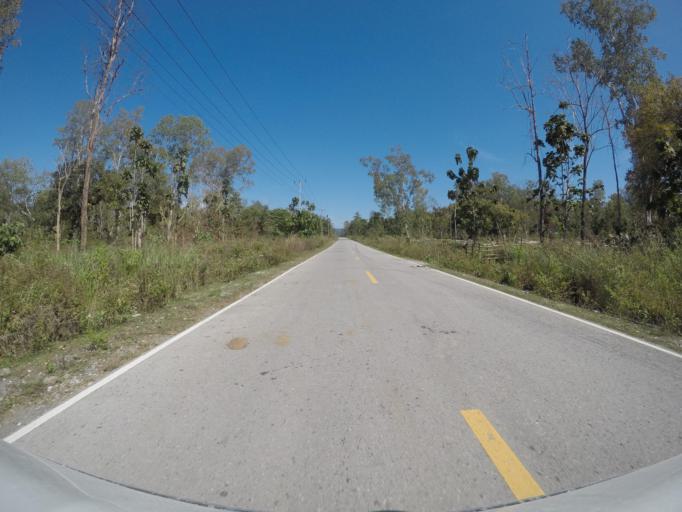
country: TL
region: Viqueque
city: Viqueque
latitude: -8.9717
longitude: 126.0330
